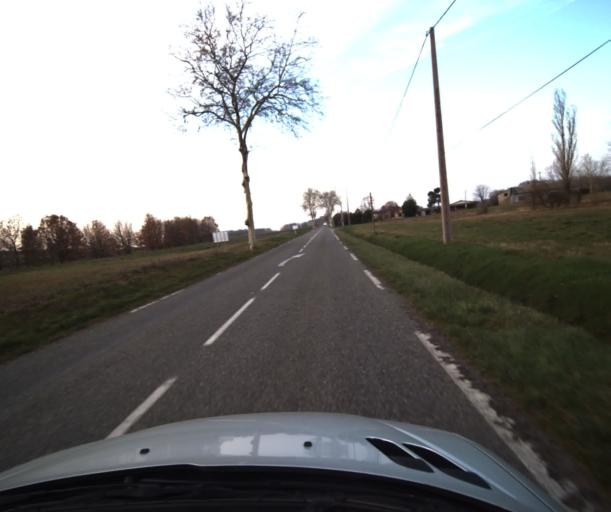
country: FR
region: Midi-Pyrenees
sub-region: Departement de la Haute-Garonne
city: Fronton
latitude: 43.8721
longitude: 1.3797
